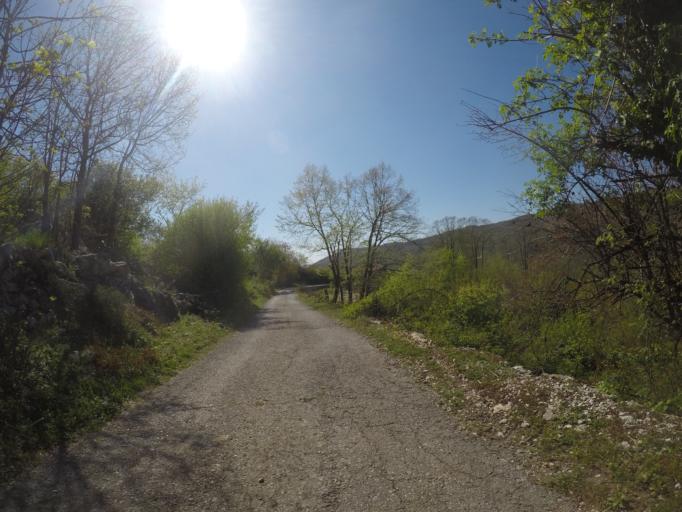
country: ME
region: Danilovgrad
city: Danilovgrad
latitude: 42.5218
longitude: 19.0501
